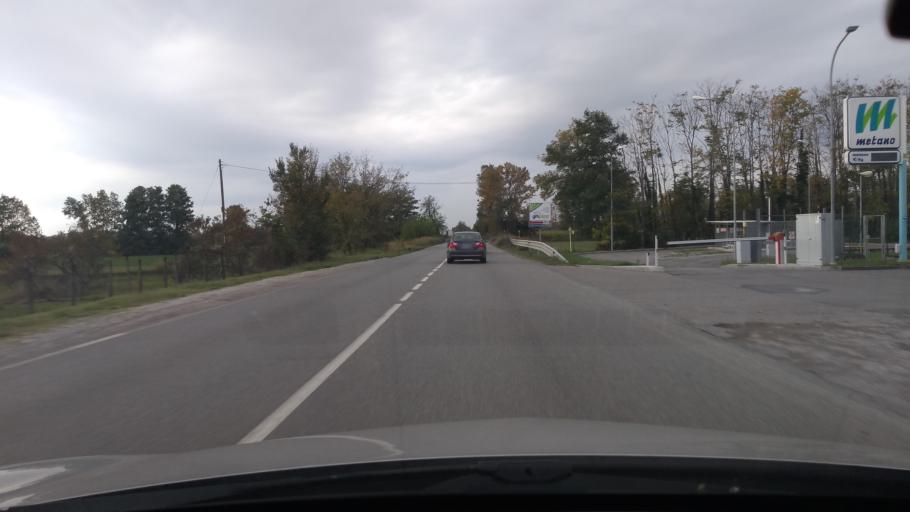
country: IT
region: Lombardy
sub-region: Provincia di Bergamo
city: Spirano
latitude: 45.5926
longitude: 9.6791
